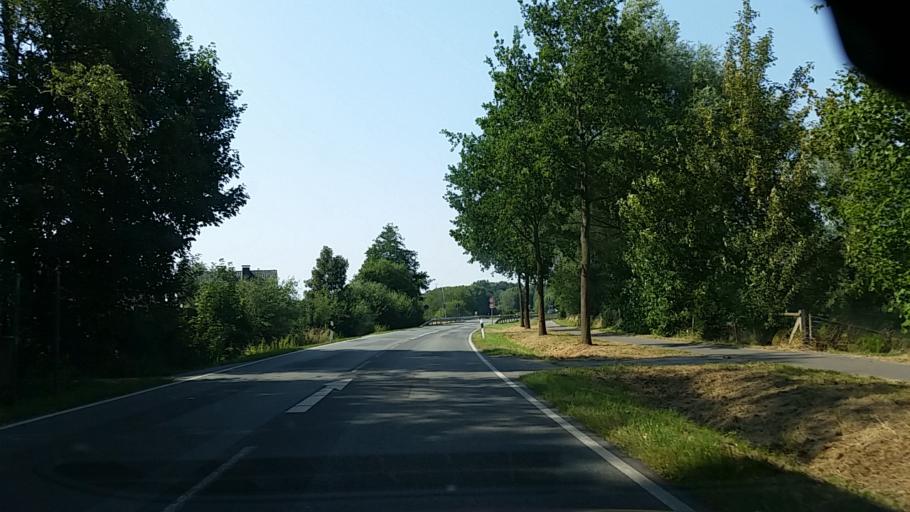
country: DE
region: Schleswig-Holstein
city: Dahmker
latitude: 53.5988
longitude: 10.4486
